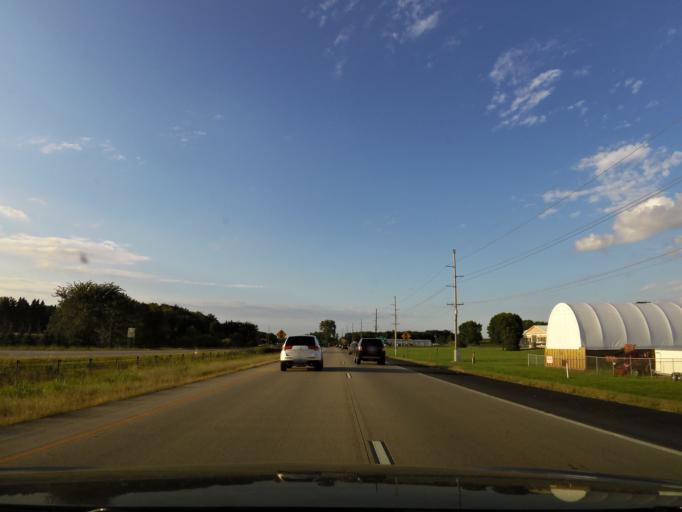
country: US
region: Minnesota
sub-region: Dakota County
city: Hastings
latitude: 44.7730
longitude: -92.8630
